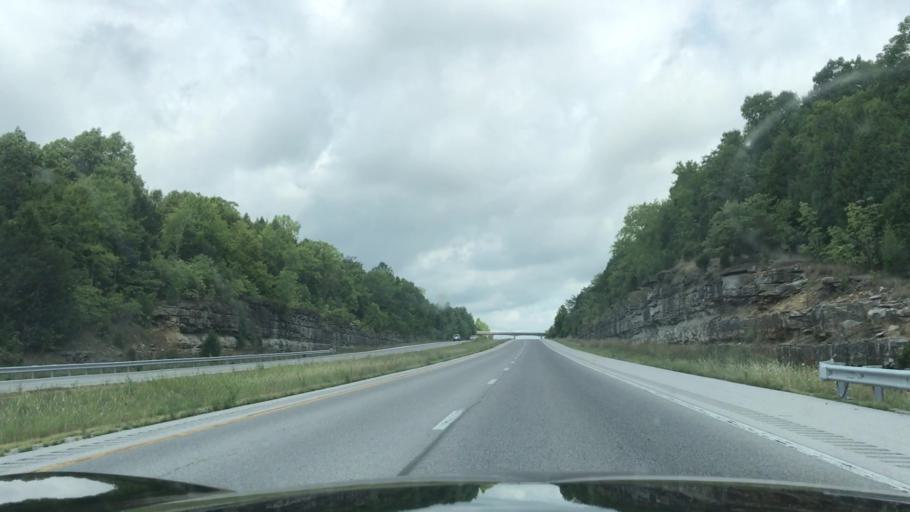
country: US
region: Kentucky
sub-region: Warren County
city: Bowling Green
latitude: 37.0233
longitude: -86.5296
